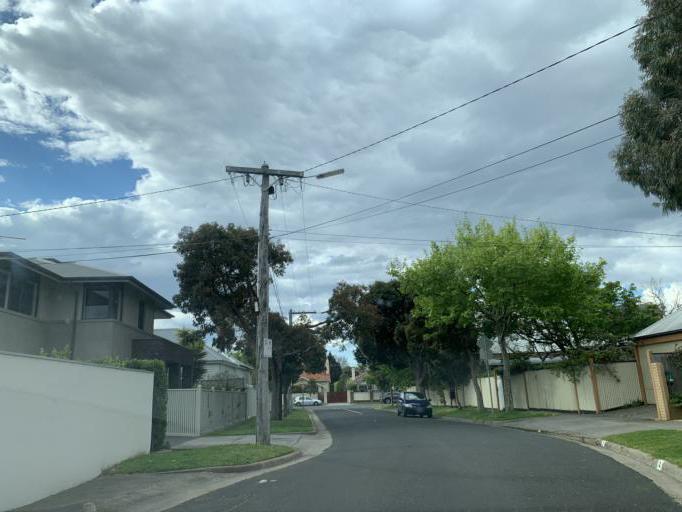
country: AU
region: Victoria
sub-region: Bayside
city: Hampton
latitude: -37.9343
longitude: 145.0012
